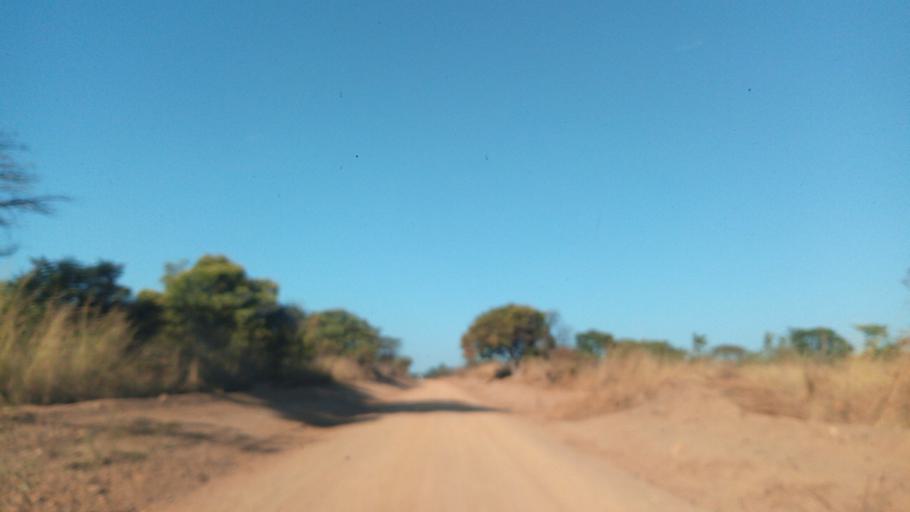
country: ZM
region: Luapula
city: Mwense
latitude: -10.4657
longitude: 28.5208
